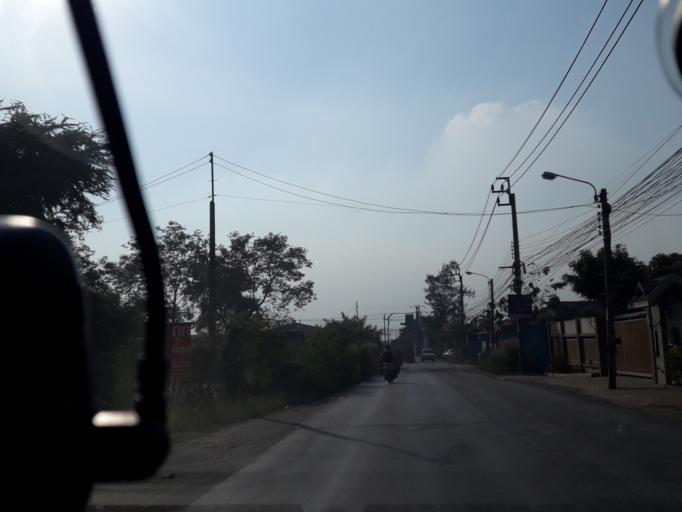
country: TH
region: Pathum Thani
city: Lam Luk Ka
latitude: 13.9108
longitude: 100.7235
